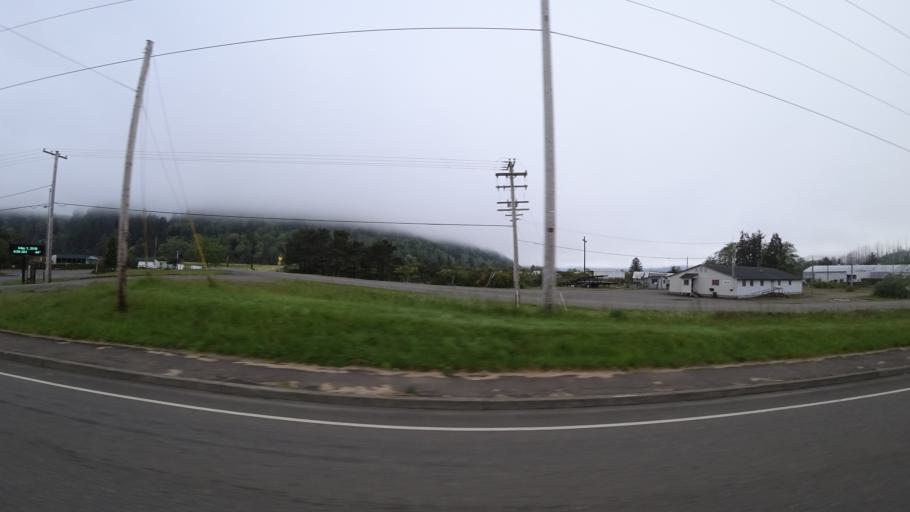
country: US
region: Oregon
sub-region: Douglas County
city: Reedsport
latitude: 43.7041
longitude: -124.1046
